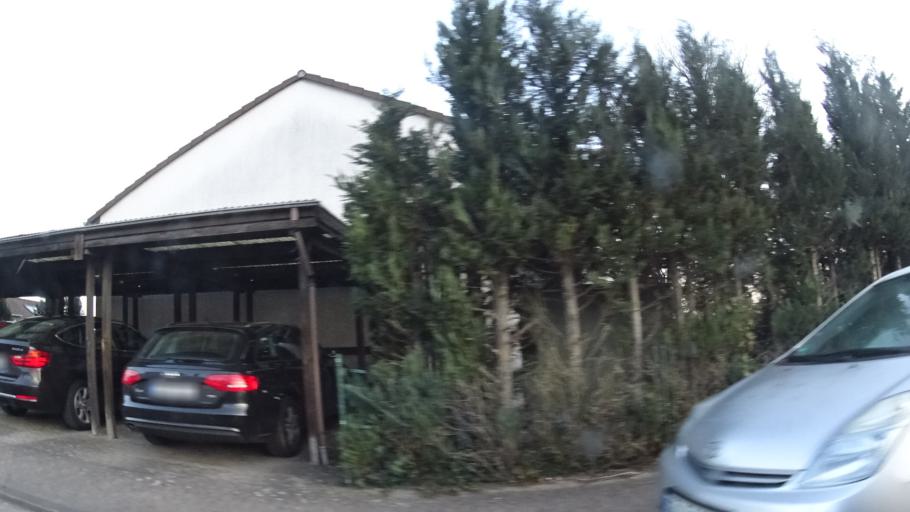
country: DE
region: Saarland
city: Sulzbach
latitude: 49.2676
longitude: 7.0343
